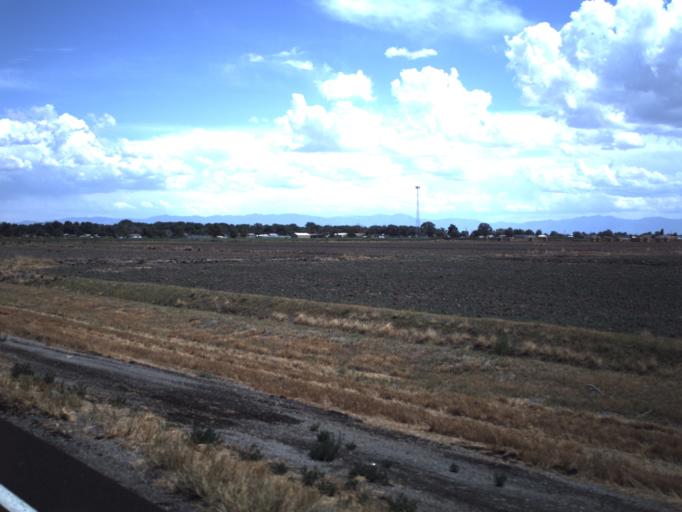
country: US
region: Utah
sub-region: Millard County
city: Delta
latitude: 39.3308
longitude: -112.6884
